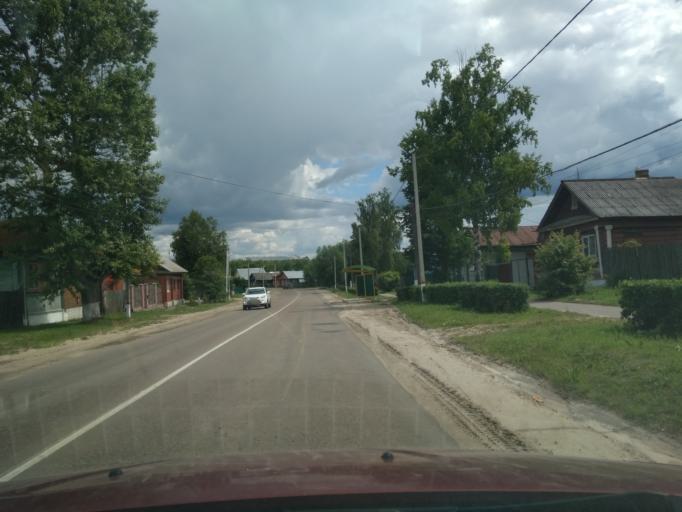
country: RU
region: Vladimir
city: Melenki
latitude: 55.3389
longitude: 41.6170
